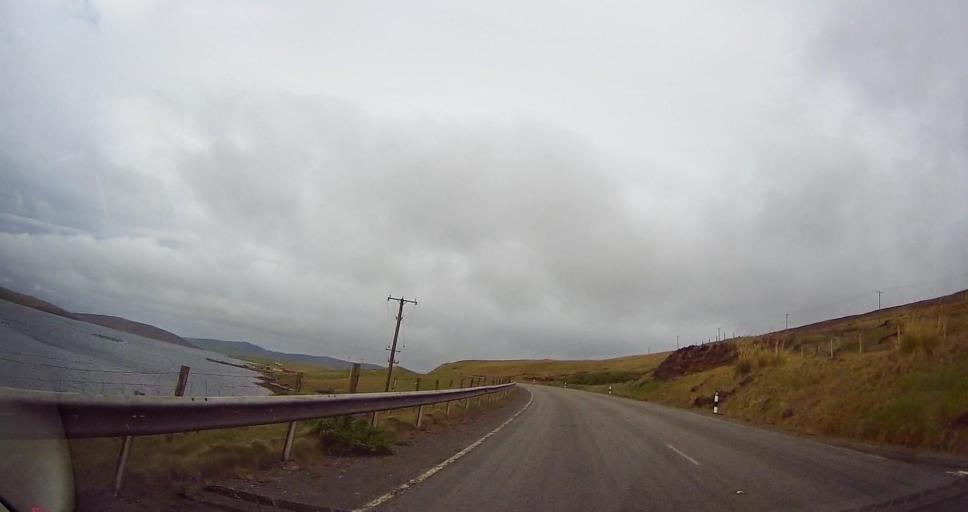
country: GB
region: Scotland
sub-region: Shetland Islands
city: Lerwick
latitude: 60.3700
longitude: -1.3023
